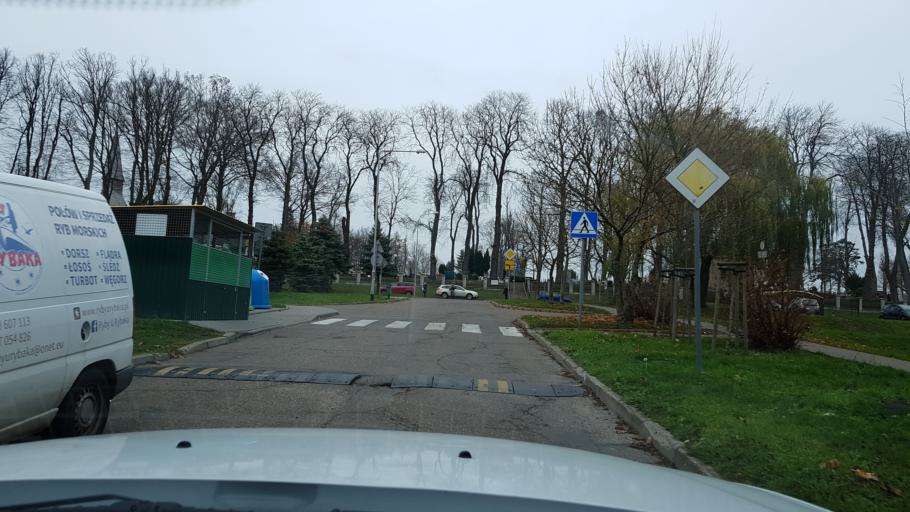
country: PL
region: West Pomeranian Voivodeship
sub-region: Powiat slawienski
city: Darlowo
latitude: 54.4234
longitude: 16.4169
